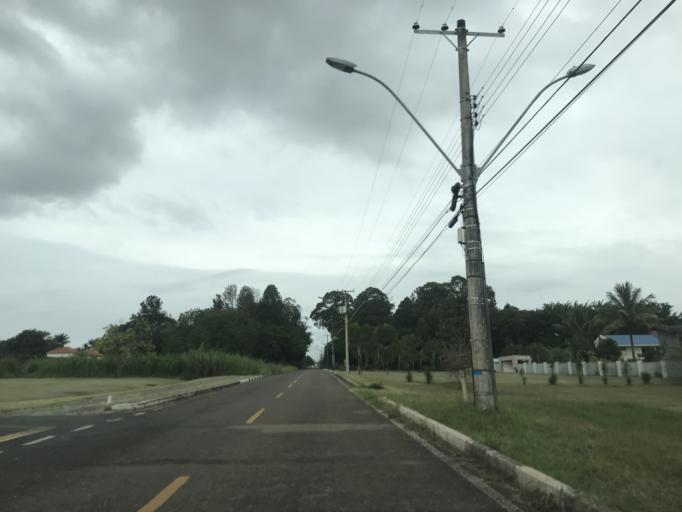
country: BR
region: Federal District
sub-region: Brasilia
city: Brasilia
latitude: -15.8922
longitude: -47.9310
